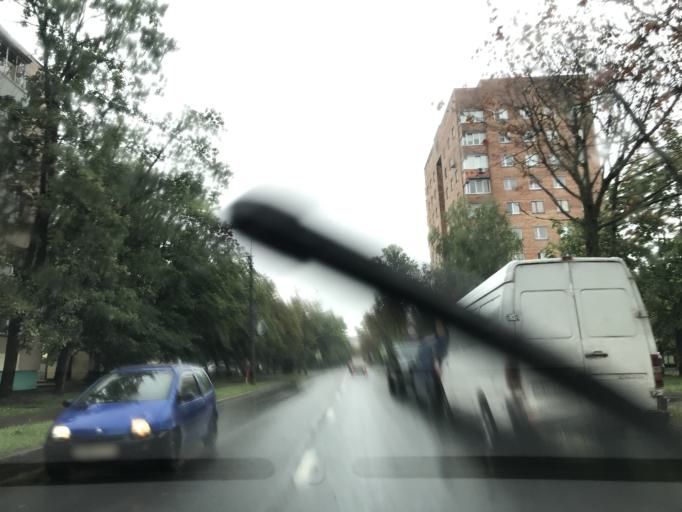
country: BY
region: Minsk
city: Bal'shavik
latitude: 53.9523
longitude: 27.6090
